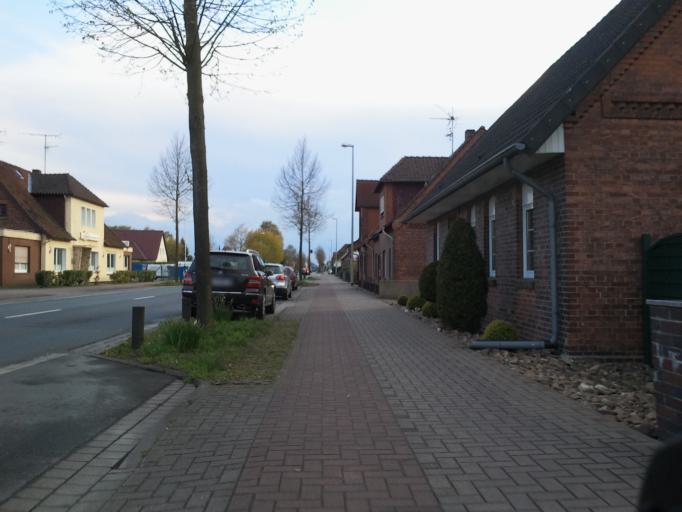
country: DE
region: Lower Saxony
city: Nienburg
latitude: 52.6588
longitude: 9.2336
